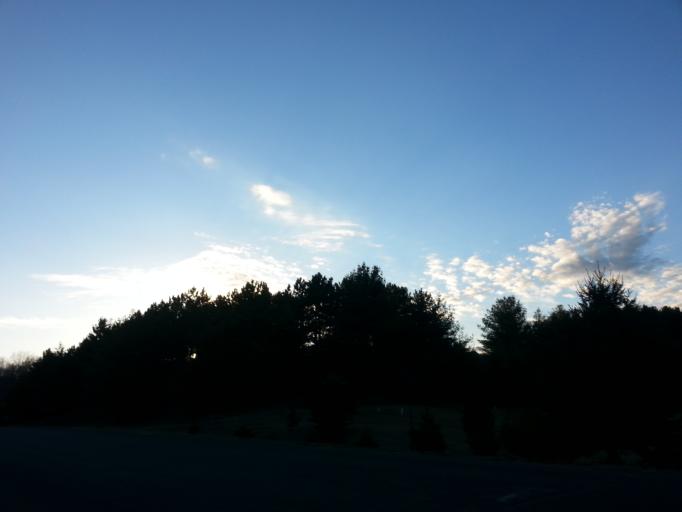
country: US
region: Minnesota
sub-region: Washington County
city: Lake Elmo
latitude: 44.9787
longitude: -92.8349
